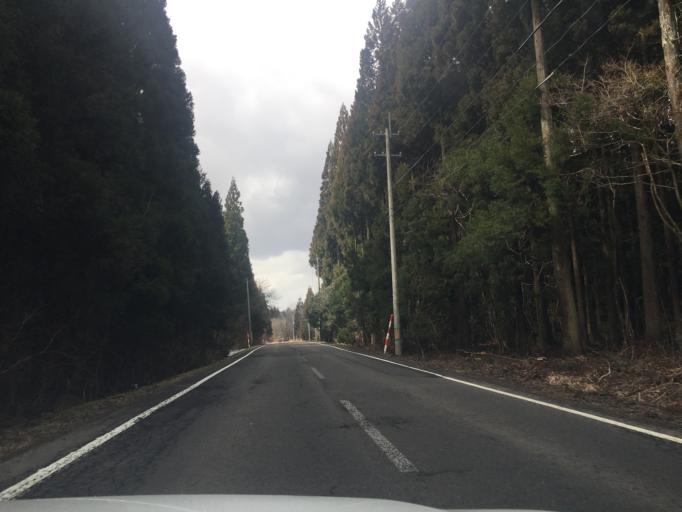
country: JP
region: Akita
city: Takanosu
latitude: 40.1797
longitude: 140.3561
